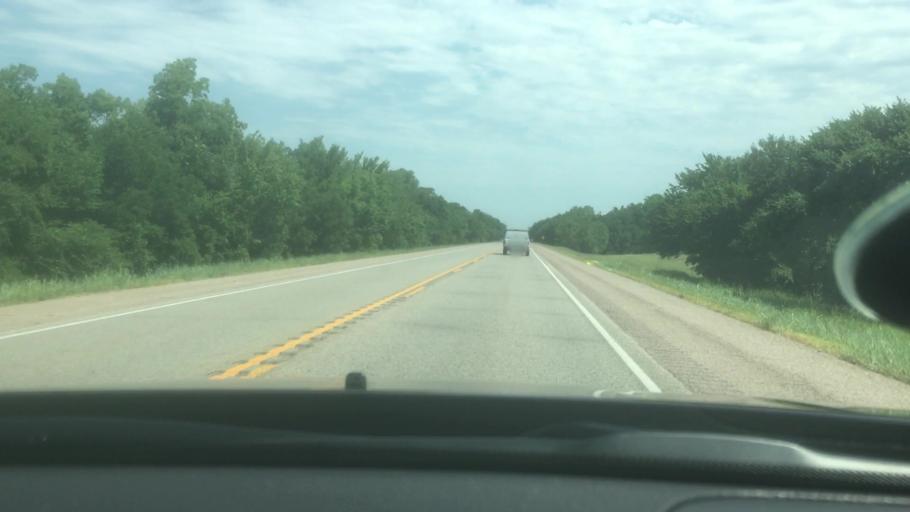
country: US
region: Oklahoma
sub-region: Seminole County
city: Maud
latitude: 35.0766
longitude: -96.9312
